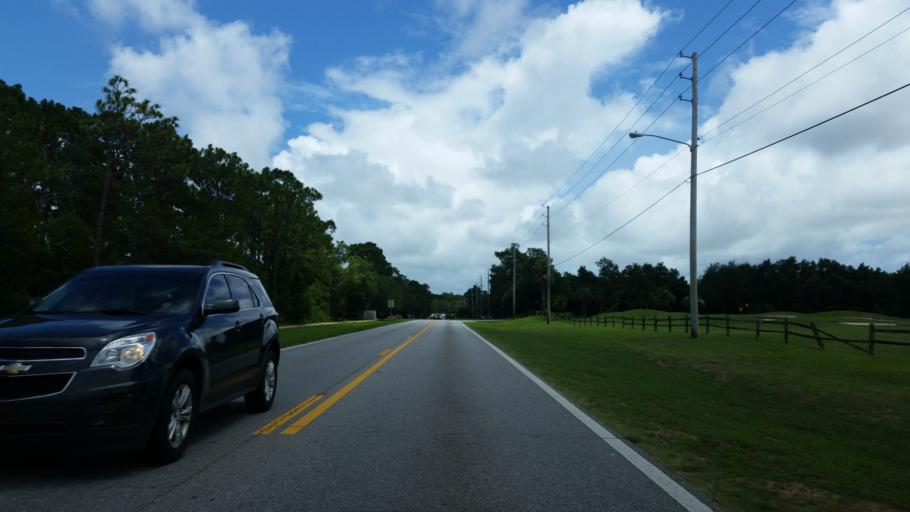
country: US
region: Florida
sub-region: Santa Rosa County
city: Holley
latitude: 30.4408
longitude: -86.9217
